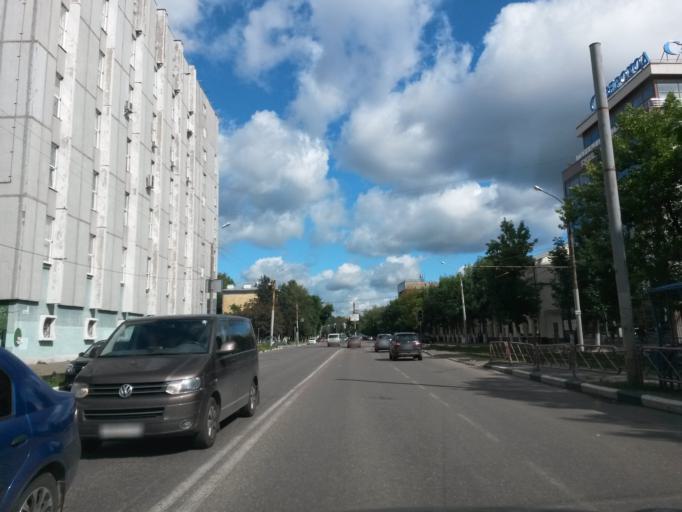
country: RU
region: Jaroslavl
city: Yaroslavl
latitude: 57.6307
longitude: 39.8698
